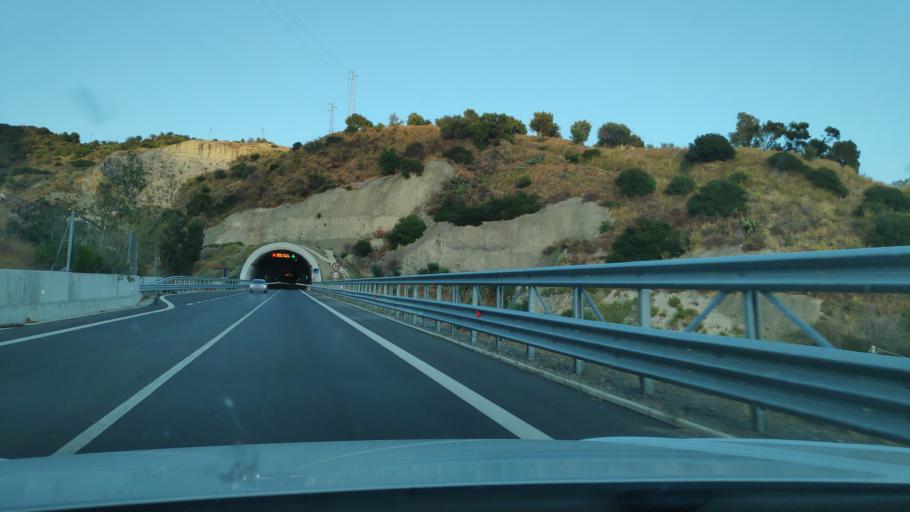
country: IT
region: Calabria
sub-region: Provincia di Reggio Calabria
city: Palizzi Marina
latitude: 37.9236
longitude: 15.9846
